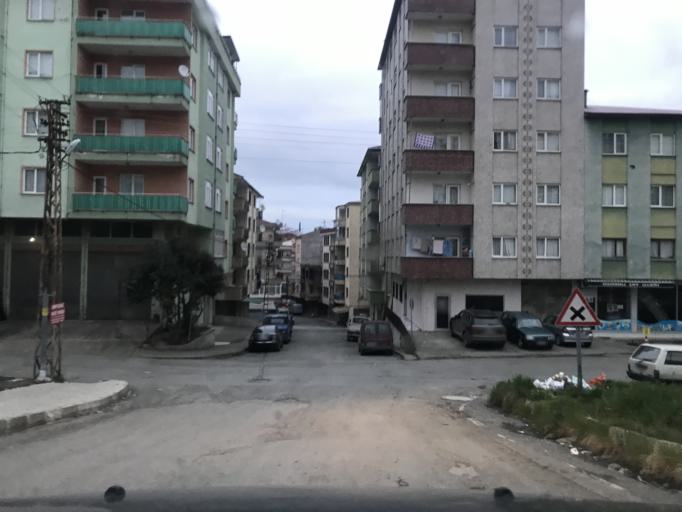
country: TR
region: Trabzon
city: Akcaabat
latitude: 41.0146
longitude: 39.5904
